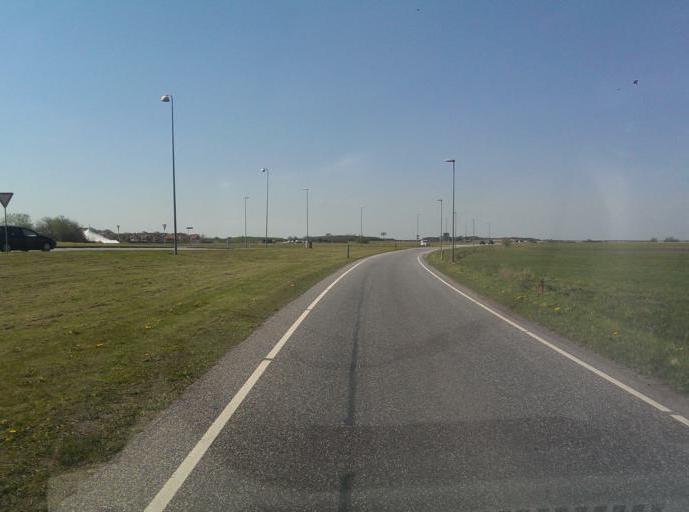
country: DK
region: South Denmark
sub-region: Esbjerg Kommune
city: Ribe
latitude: 55.3356
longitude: 8.7684
